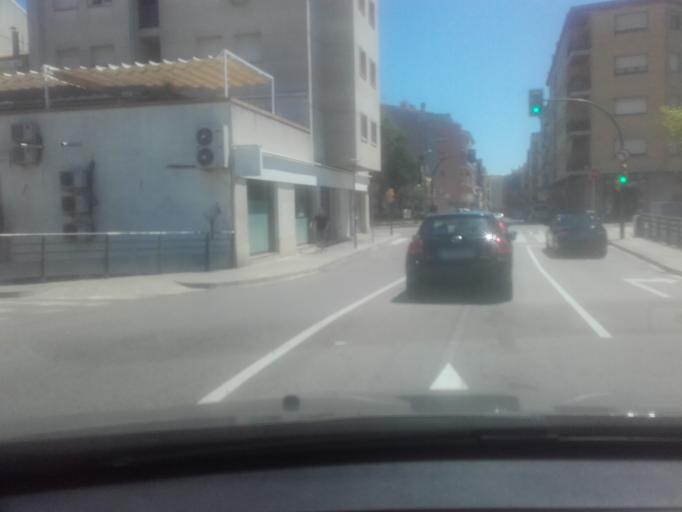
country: ES
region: Catalonia
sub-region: Provincia de Tarragona
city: El Vendrell
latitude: 41.2211
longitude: 1.5281
